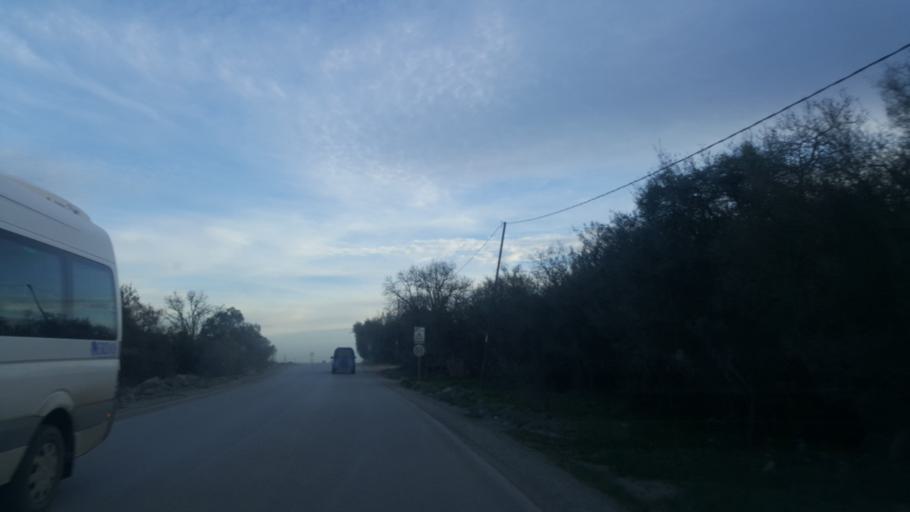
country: TR
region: Kocaeli
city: Tavsanli
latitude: 40.8518
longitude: 29.5553
